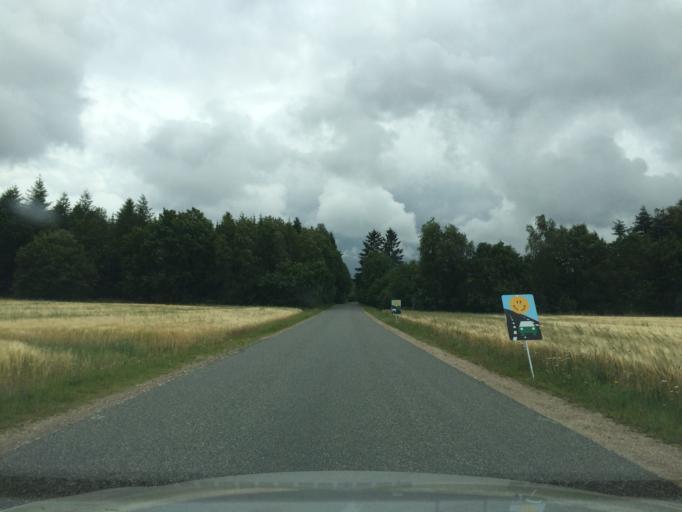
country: DK
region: Central Jutland
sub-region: Silkeborg Kommune
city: Svejbaek
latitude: 56.1992
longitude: 9.7069
